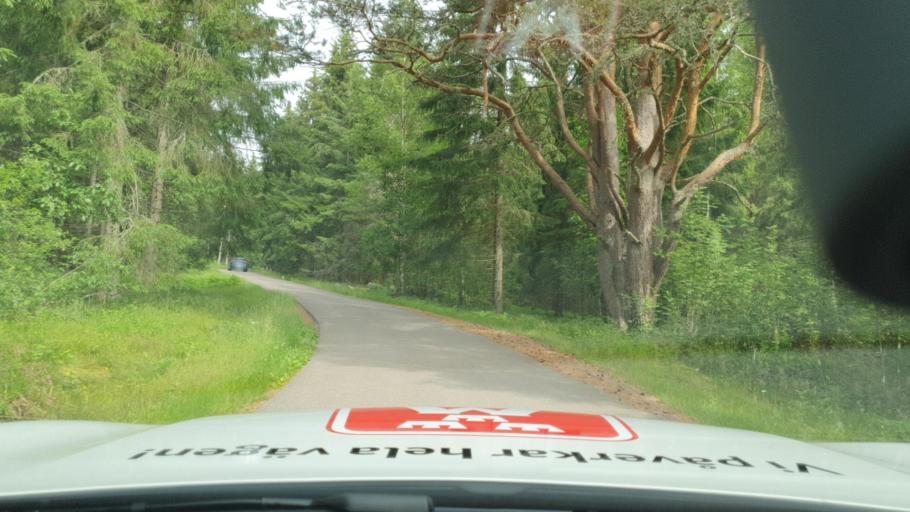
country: SE
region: Vaermland
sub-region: Sunne Kommun
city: Sunne
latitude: 59.9695
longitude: 13.1011
